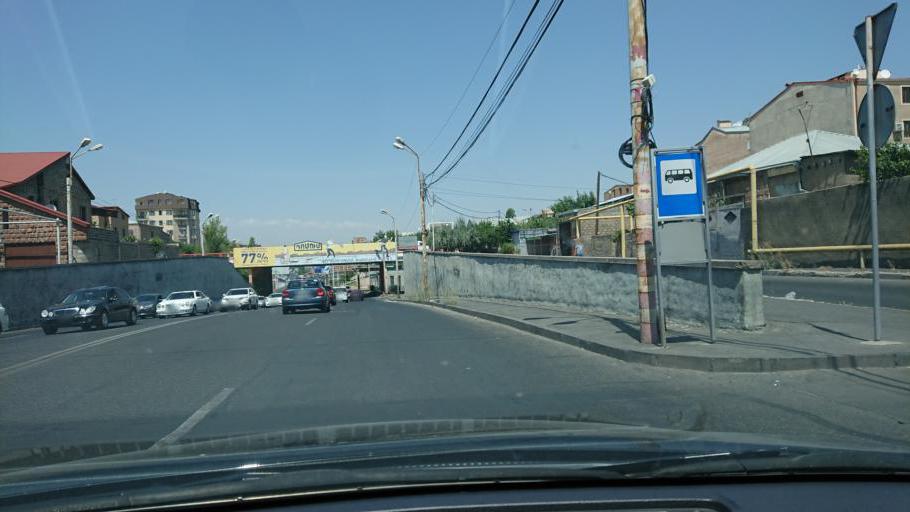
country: AM
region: Yerevan
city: Yerevan
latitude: 40.2056
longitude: 44.4969
